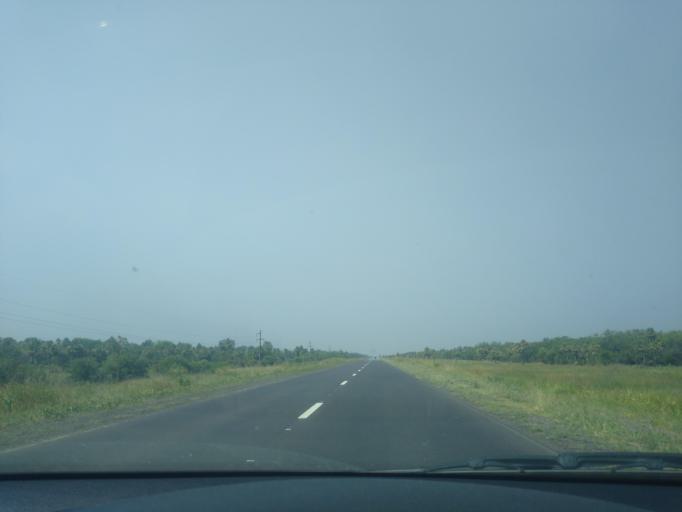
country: AR
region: Chaco
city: Fontana
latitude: -27.5189
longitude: -59.1046
